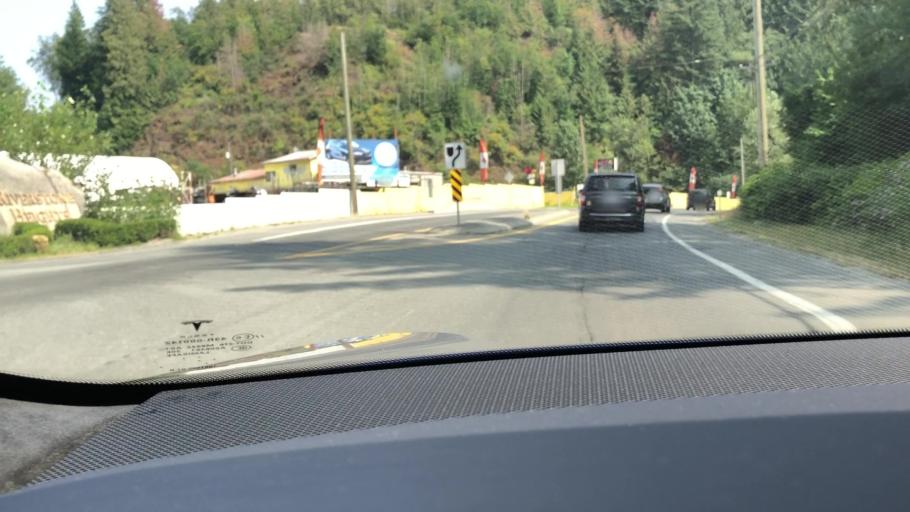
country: CA
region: British Columbia
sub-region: Fraser Valley Regional District
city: Chilliwack
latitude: 49.0919
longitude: -121.9687
